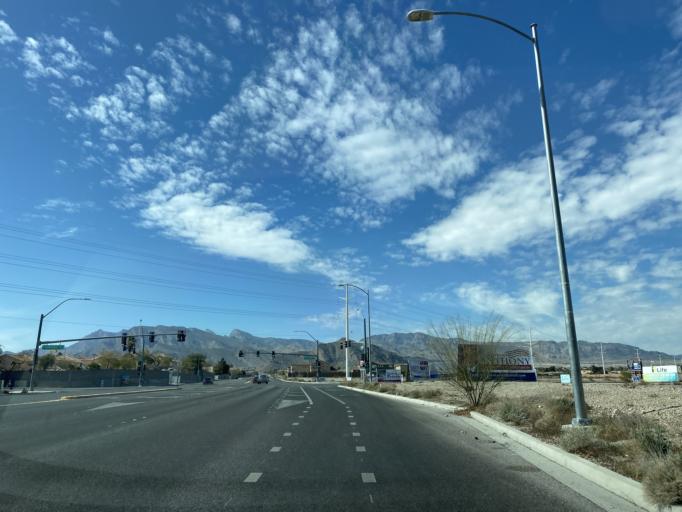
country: US
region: Nevada
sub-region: Clark County
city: Summerlin South
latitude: 36.2338
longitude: -115.2780
